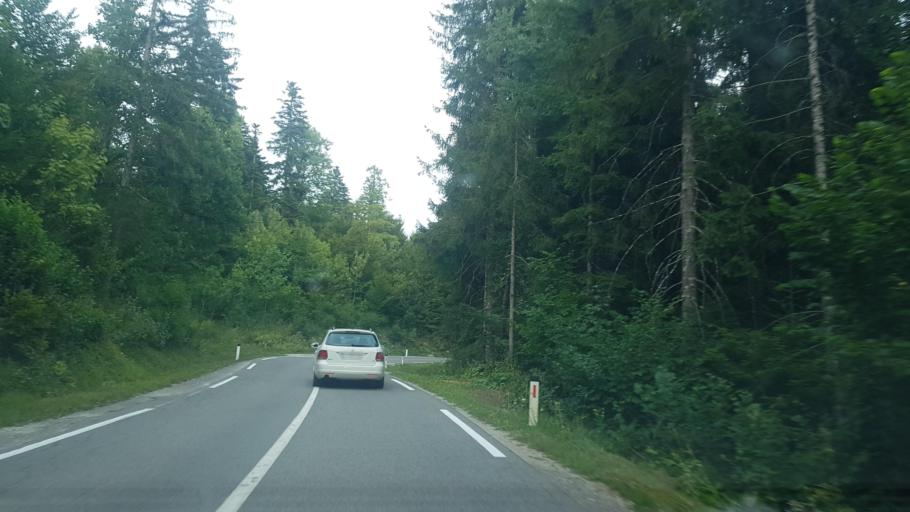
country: SI
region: Logatec
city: Logatec
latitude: 45.8958
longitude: 14.1770
